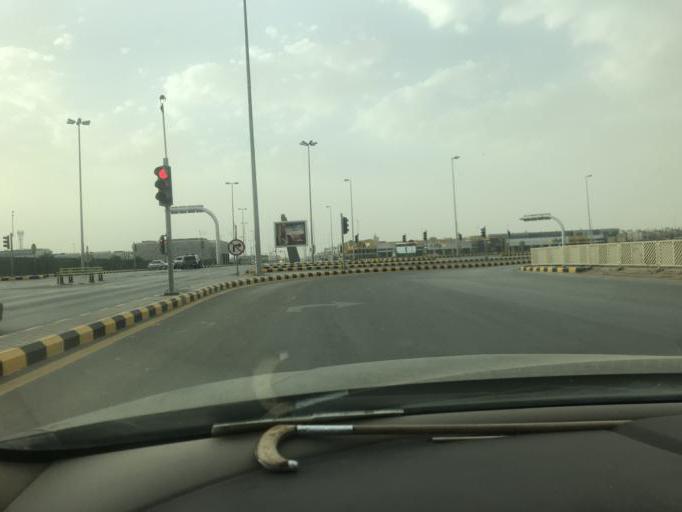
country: SA
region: Ar Riyad
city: Riyadh
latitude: 24.8003
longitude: 46.6535
